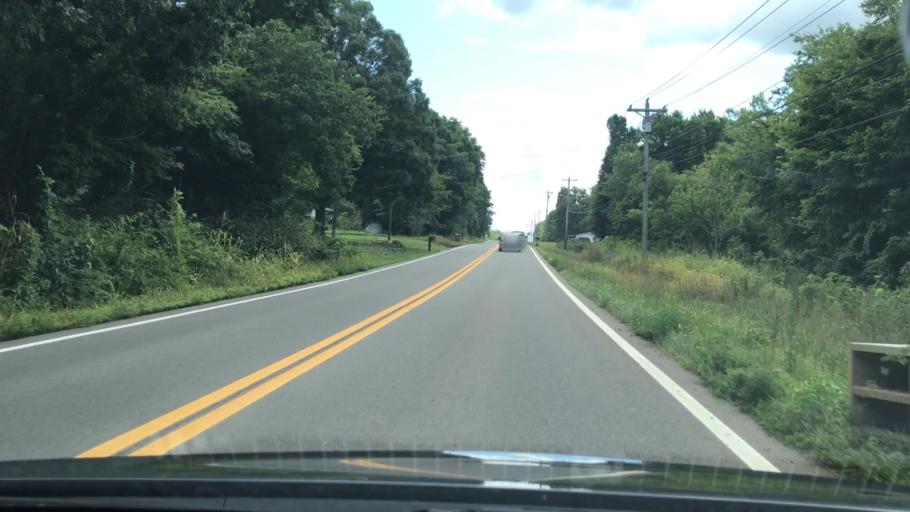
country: US
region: Tennessee
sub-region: Williamson County
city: Nolensville
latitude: 35.8508
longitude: -86.5912
